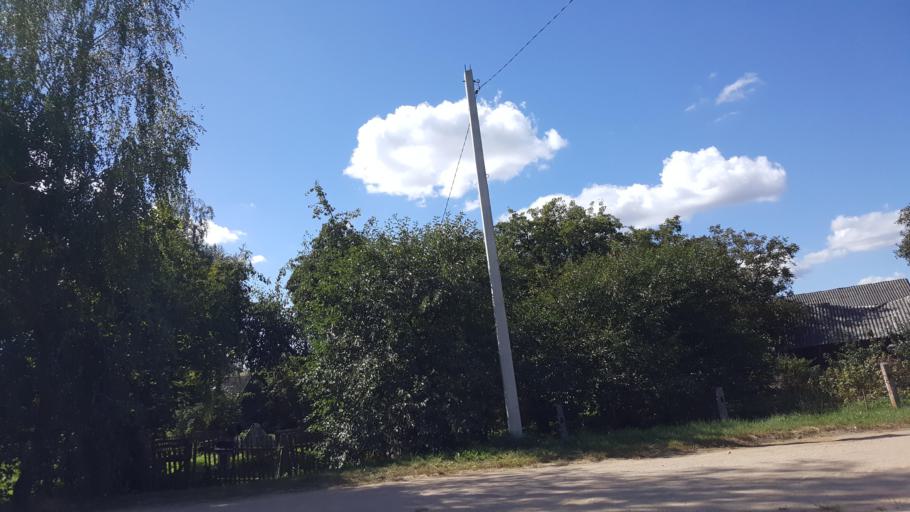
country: BY
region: Brest
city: Vysokaye
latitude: 52.2593
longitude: 23.4198
